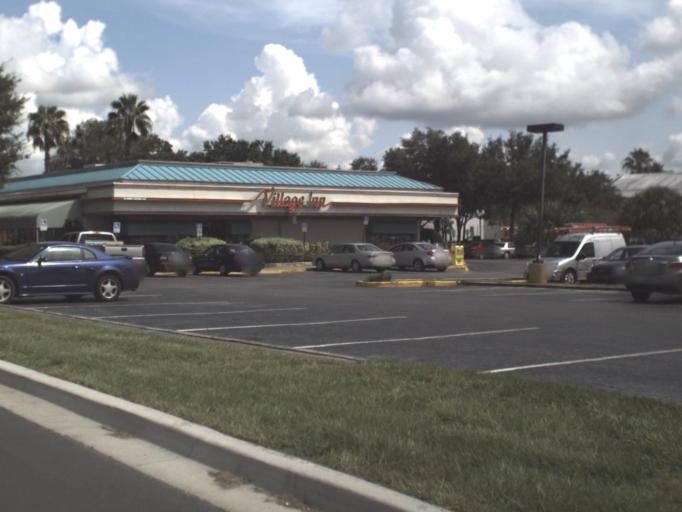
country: US
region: Florida
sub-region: Pasco County
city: Zephyrhills
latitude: 28.2329
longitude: -82.1813
